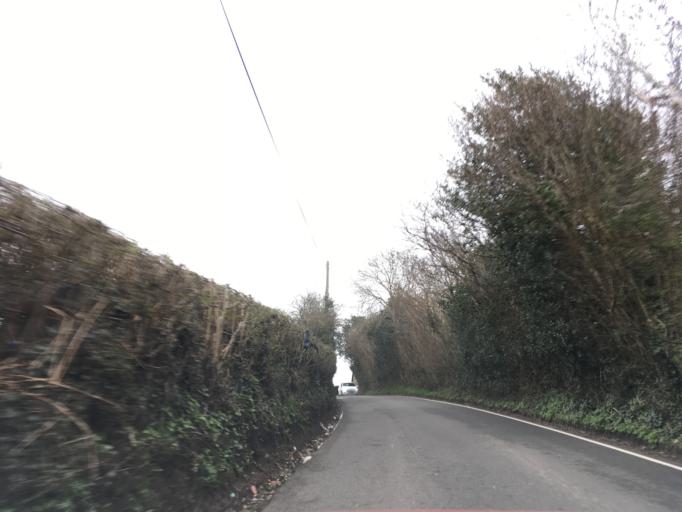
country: GB
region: Wales
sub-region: Caerphilly County Borough
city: Machen
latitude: 51.5380
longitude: -3.1484
